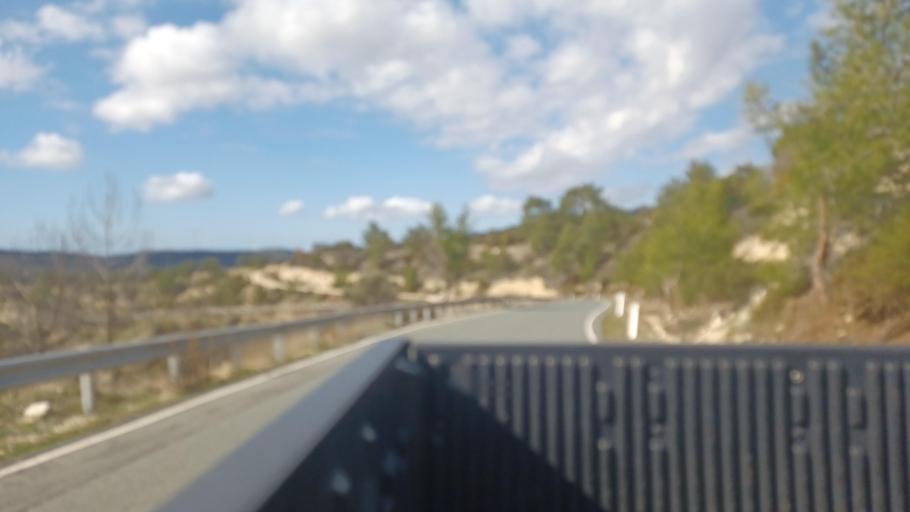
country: CY
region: Limassol
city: Pissouri
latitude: 34.7535
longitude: 32.6831
